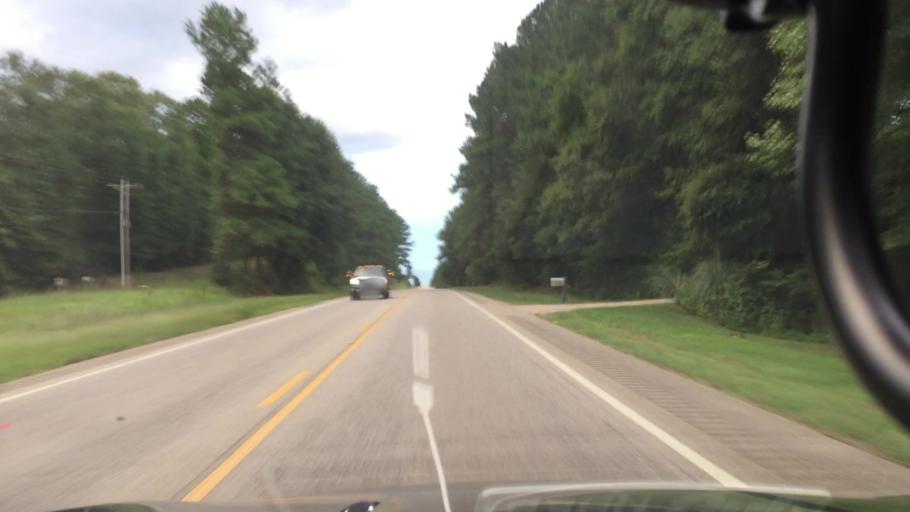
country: US
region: Alabama
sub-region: Pike County
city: Troy
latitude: 31.6614
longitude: -85.9528
